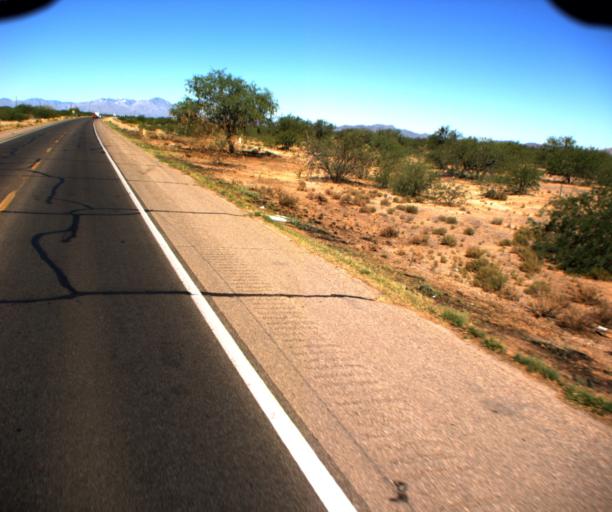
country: US
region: Arizona
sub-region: Pima County
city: Valencia West
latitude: 32.1184
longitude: -111.2094
